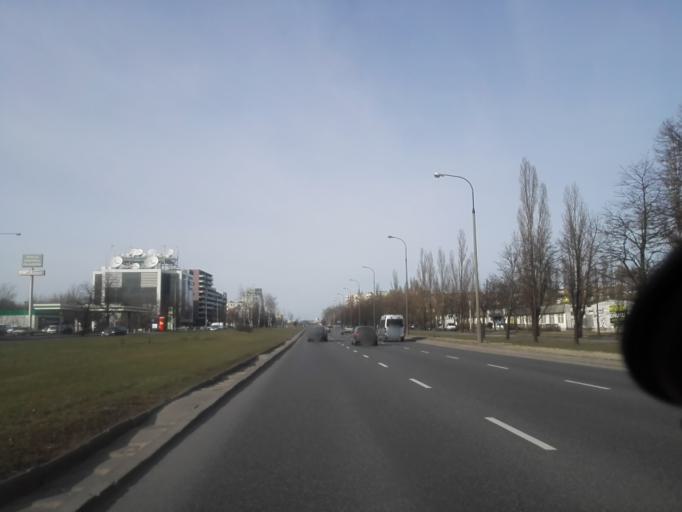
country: PL
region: Masovian Voivodeship
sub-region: Warszawa
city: Mokotow
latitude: 52.1787
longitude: 21.0449
